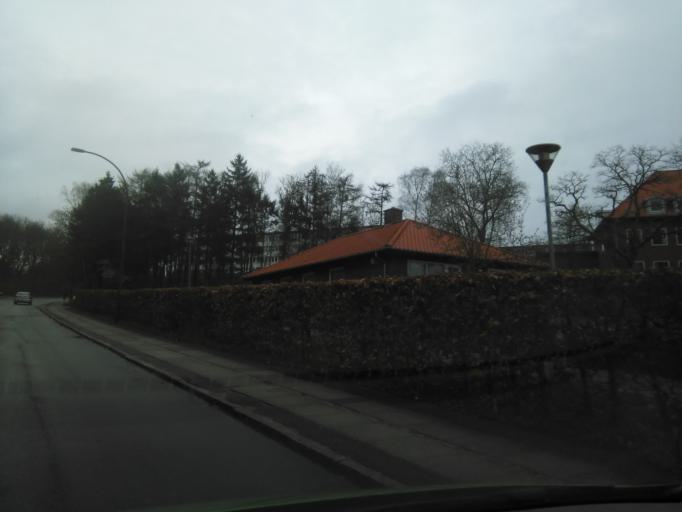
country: DK
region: Central Jutland
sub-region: Arhus Kommune
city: Stavtrup
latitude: 56.1572
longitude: 10.1252
